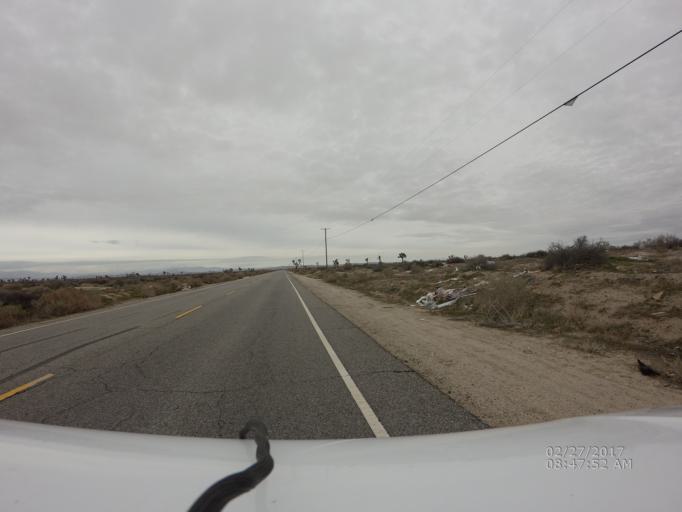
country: US
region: California
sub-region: Los Angeles County
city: Lancaster
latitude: 34.7259
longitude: -118.0770
